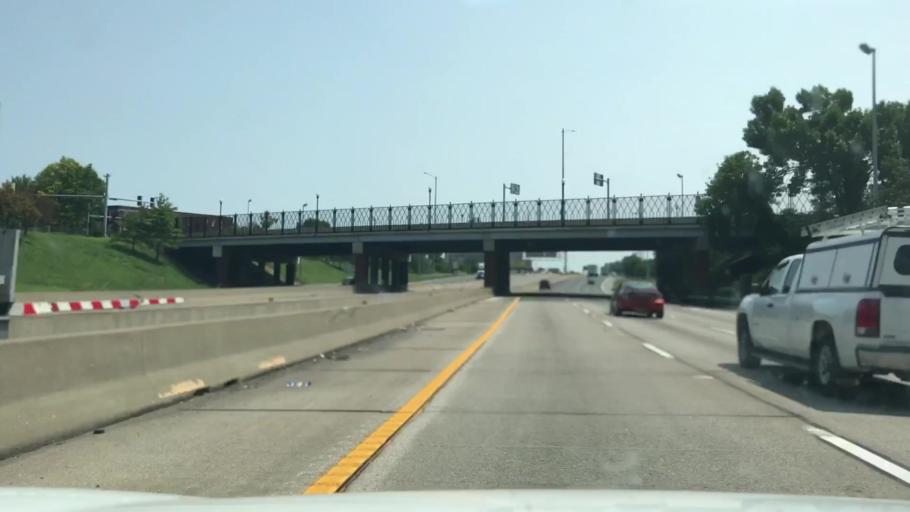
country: US
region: Missouri
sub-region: Saint Louis County
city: Pine Lawn
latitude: 38.6865
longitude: -90.2467
